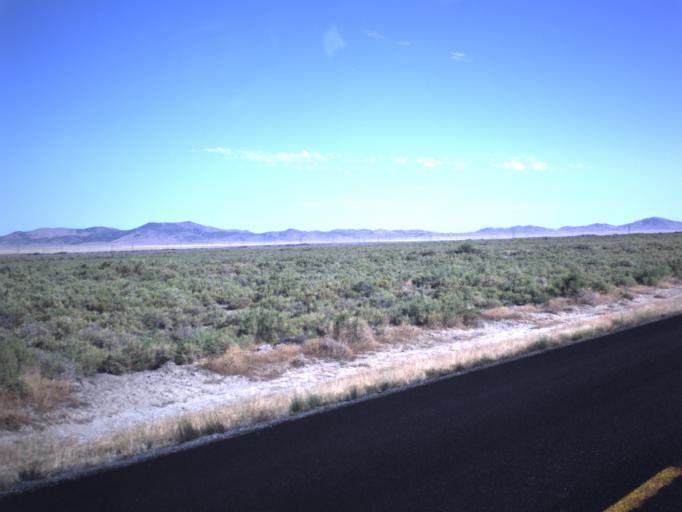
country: US
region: Utah
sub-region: Beaver County
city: Milford
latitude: 38.5488
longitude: -112.9912
